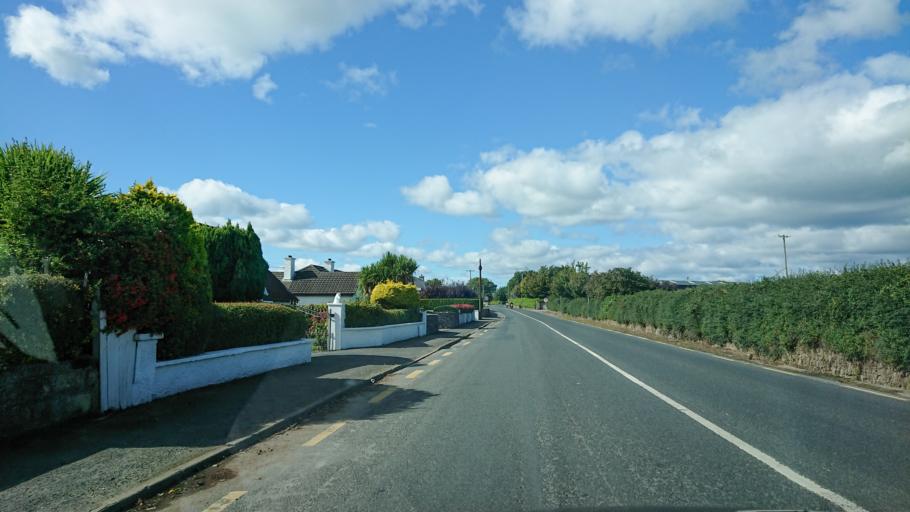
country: IE
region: Munster
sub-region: Waterford
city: Dungarvan
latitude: 52.0957
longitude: -7.6463
